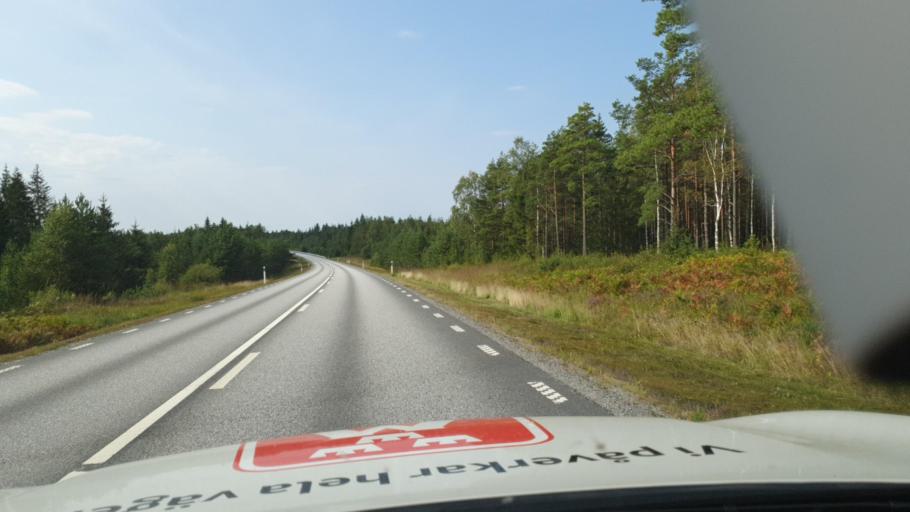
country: SE
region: Vaestra Goetaland
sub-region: Dals-Ed Kommun
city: Ed
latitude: 58.8382
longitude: 11.6223
